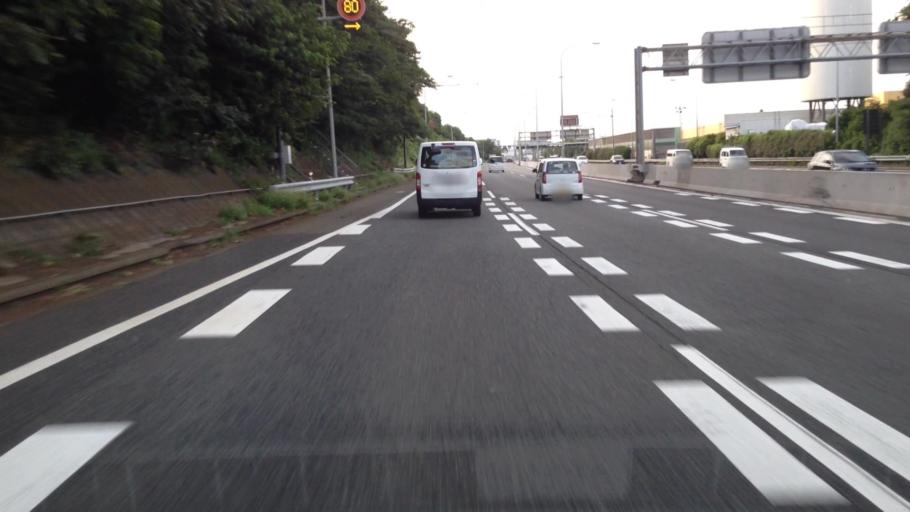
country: JP
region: Kanagawa
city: Yokohama
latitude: 35.4809
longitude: 139.5950
